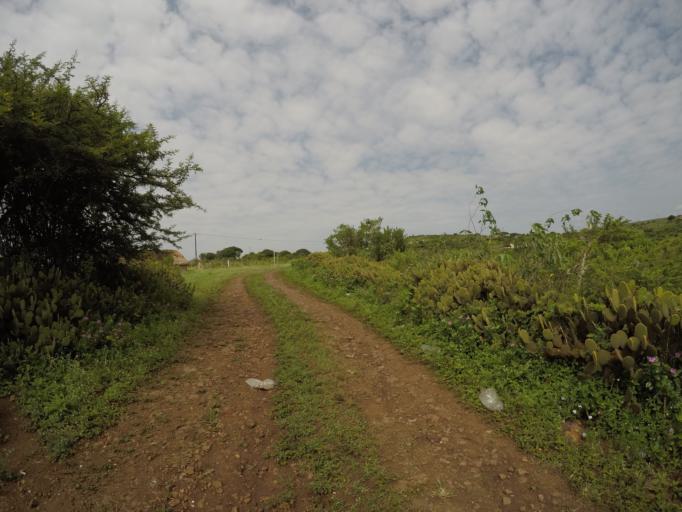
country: ZA
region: KwaZulu-Natal
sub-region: uThungulu District Municipality
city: Empangeni
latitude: -28.6218
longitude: 31.9097
